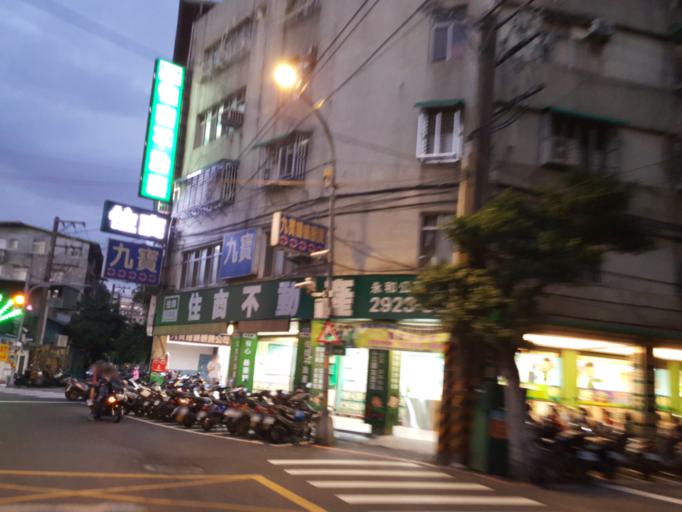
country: TW
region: Taipei
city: Taipei
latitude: 25.0013
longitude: 121.5150
